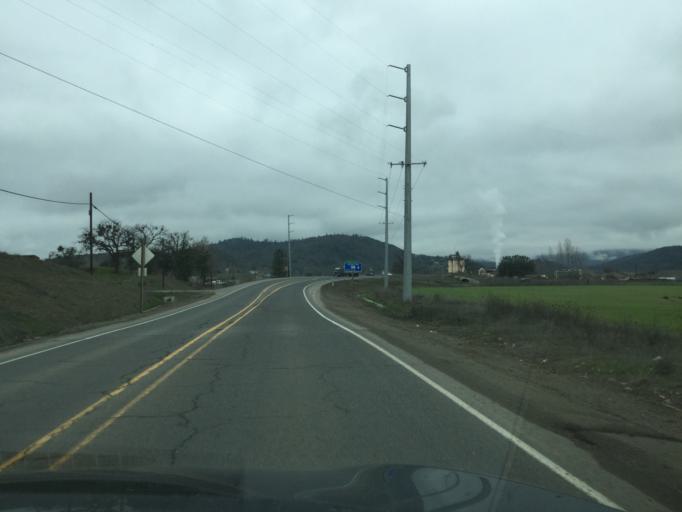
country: US
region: Oregon
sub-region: Jackson County
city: Central Point
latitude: 42.4195
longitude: -122.9544
